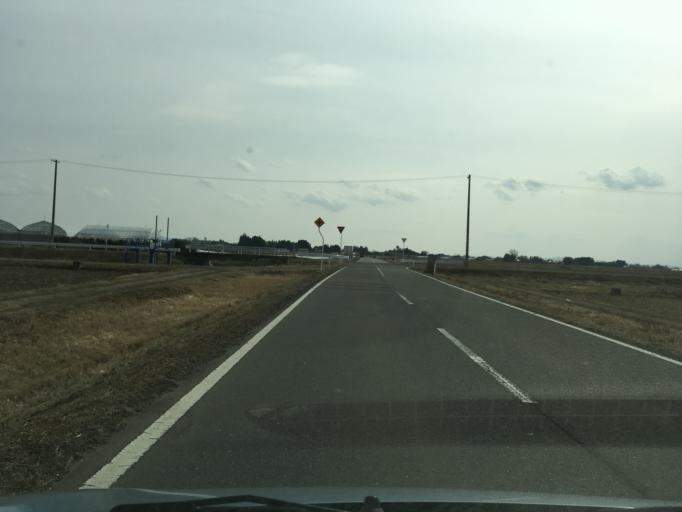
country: JP
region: Miyagi
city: Wakuya
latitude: 38.7291
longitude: 141.2396
